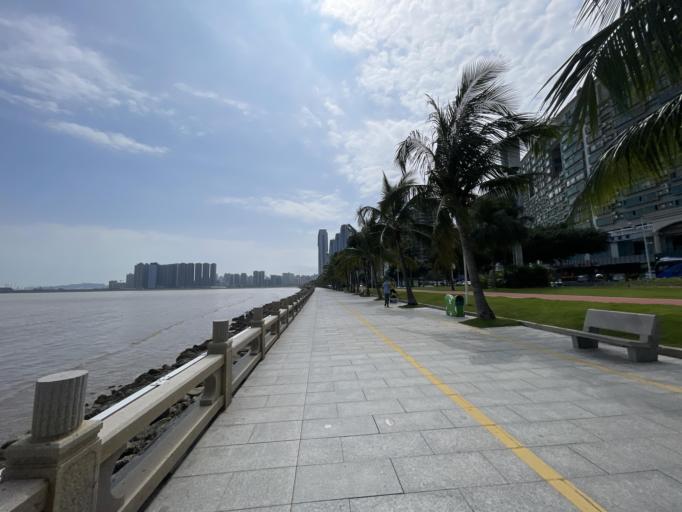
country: CN
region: Guangdong
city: Jida
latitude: 22.2297
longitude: 113.5592
